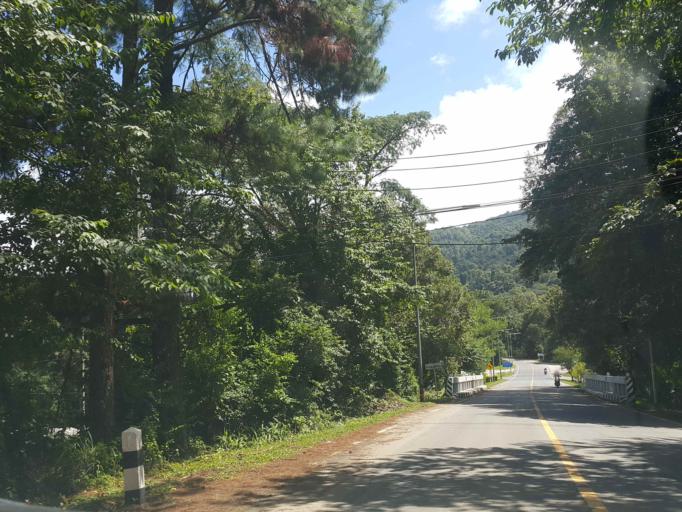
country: TH
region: Chiang Mai
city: Mae Chaem
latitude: 18.5367
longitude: 98.5235
